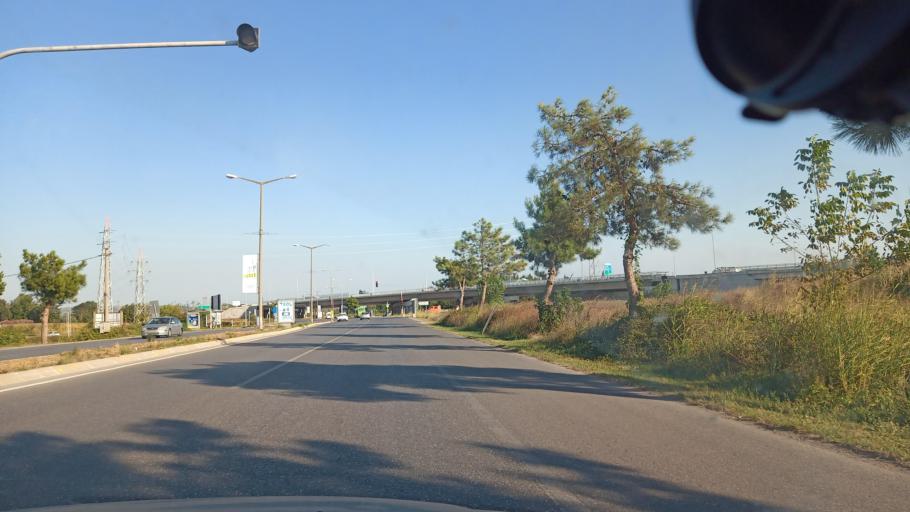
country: TR
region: Sakarya
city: Kazimpasa
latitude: 40.8458
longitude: 30.3279
